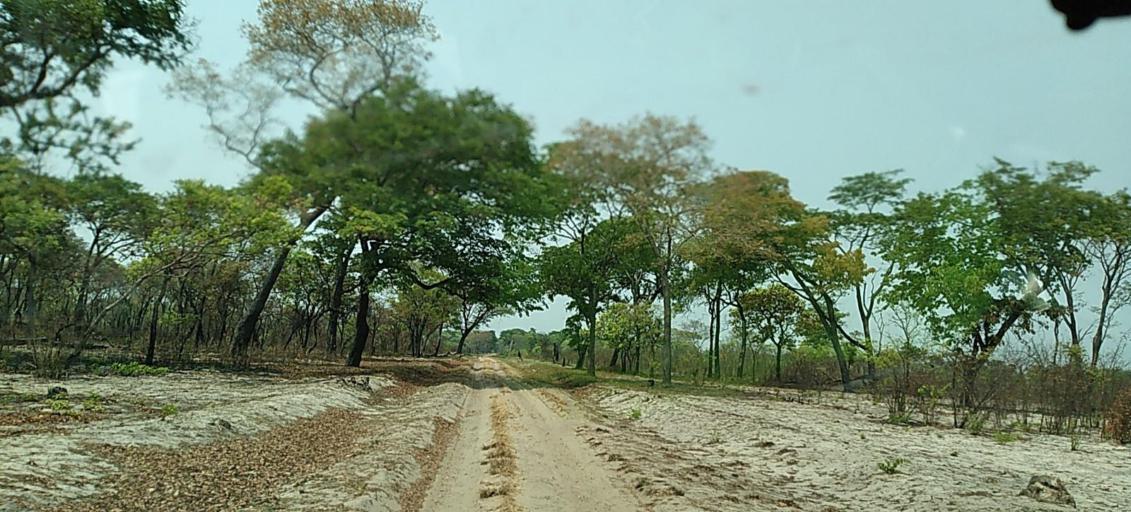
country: ZM
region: North-Western
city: Zambezi
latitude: -13.9440
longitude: 23.2229
